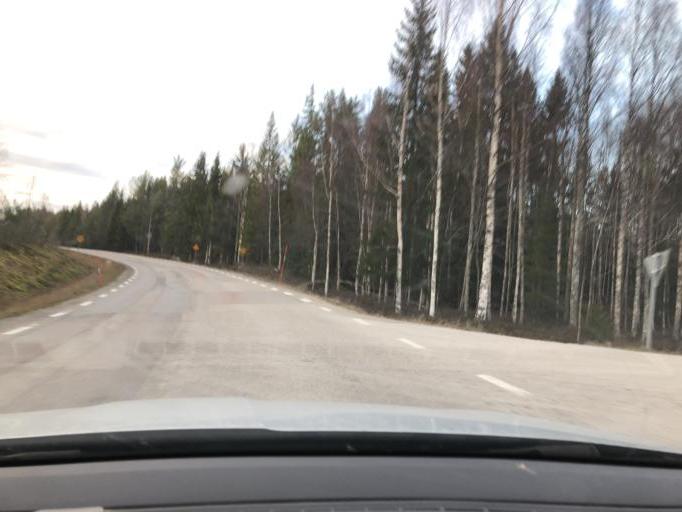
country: SE
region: Gaevleborg
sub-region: Hudiksvalls Kommun
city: Iggesund
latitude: 61.5514
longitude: 16.9903
